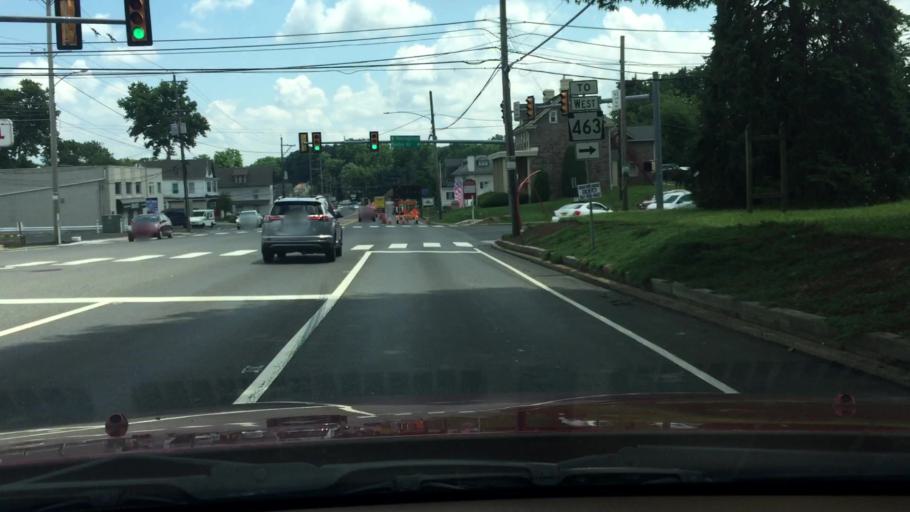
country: US
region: Pennsylvania
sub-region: Montgomery County
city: Horsham
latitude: 40.1830
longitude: -75.1318
